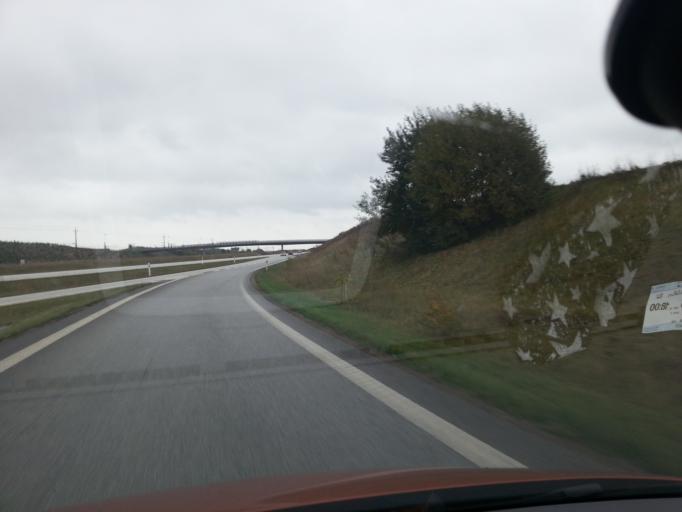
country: SE
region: Skane
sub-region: Malmo
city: Tygelsjo
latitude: 55.5469
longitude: 13.0071
